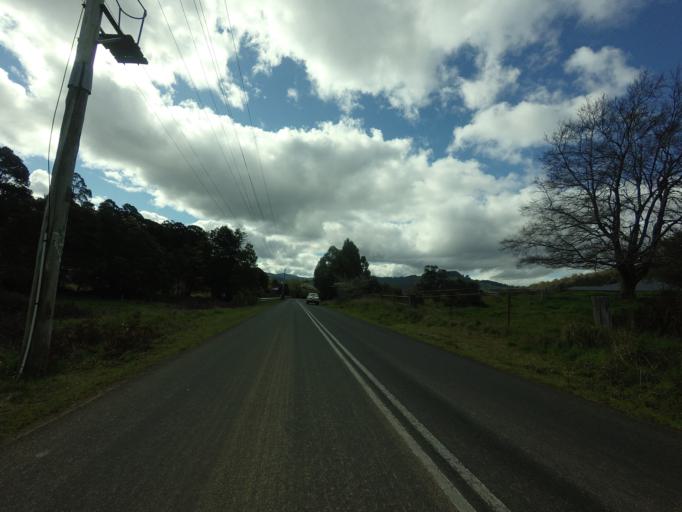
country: AU
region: Tasmania
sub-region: Huon Valley
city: Geeveston
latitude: -43.1766
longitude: 146.9238
